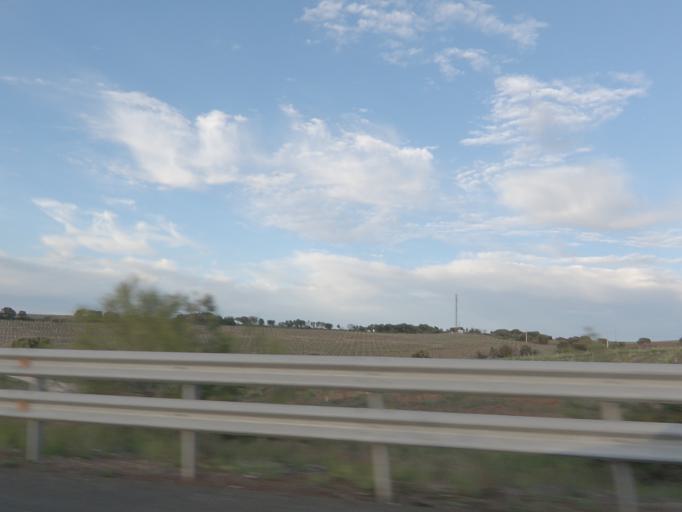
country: ES
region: Extremadura
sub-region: Provincia de Badajoz
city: Aljucen
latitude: 39.0339
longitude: -6.3364
